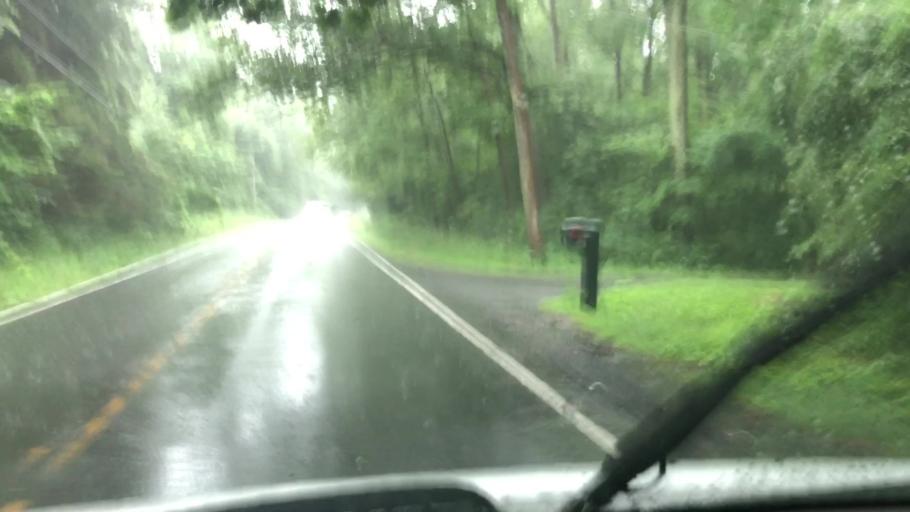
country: US
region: Massachusetts
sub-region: Berkshire County
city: Pittsfield
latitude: 42.4193
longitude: -73.2790
